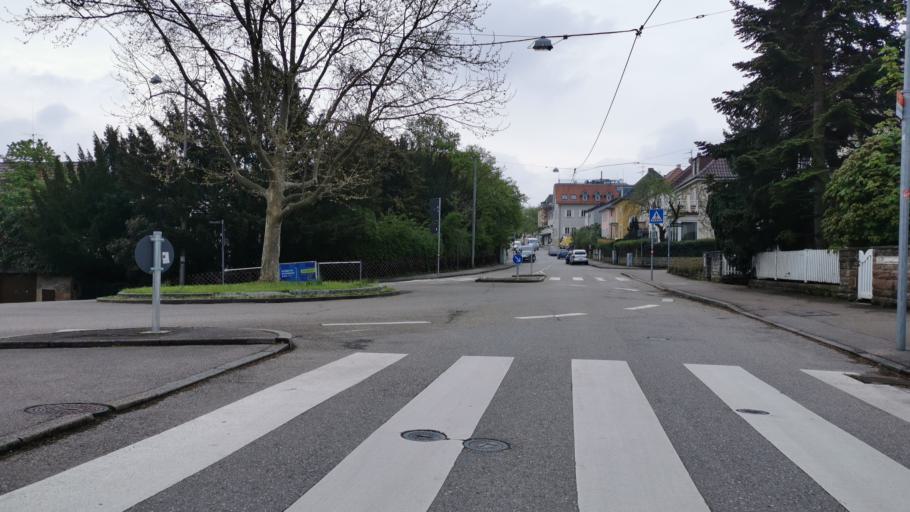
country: DE
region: Baden-Wuerttemberg
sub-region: Regierungsbezirk Stuttgart
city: Stuttgart Feuerbach
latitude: 48.8000
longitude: 9.1624
